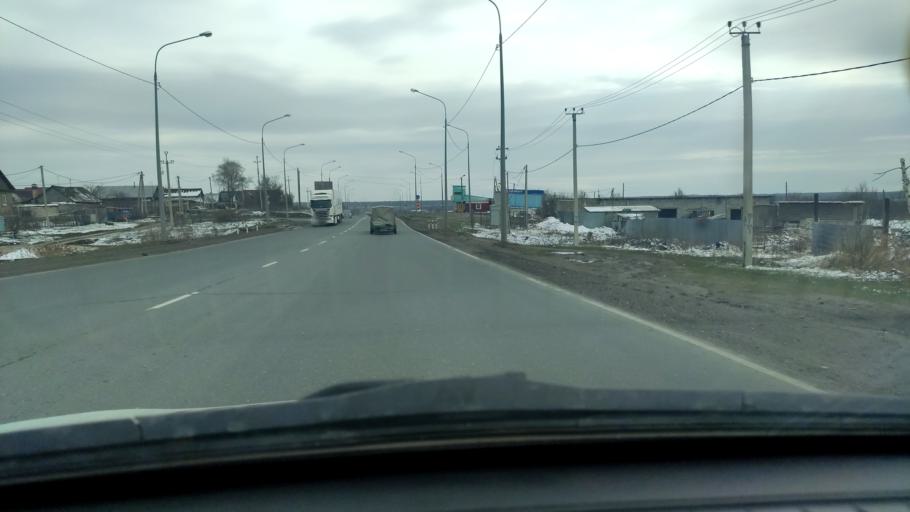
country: RU
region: Samara
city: Zhigulevsk
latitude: 53.3755
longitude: 49.4565
